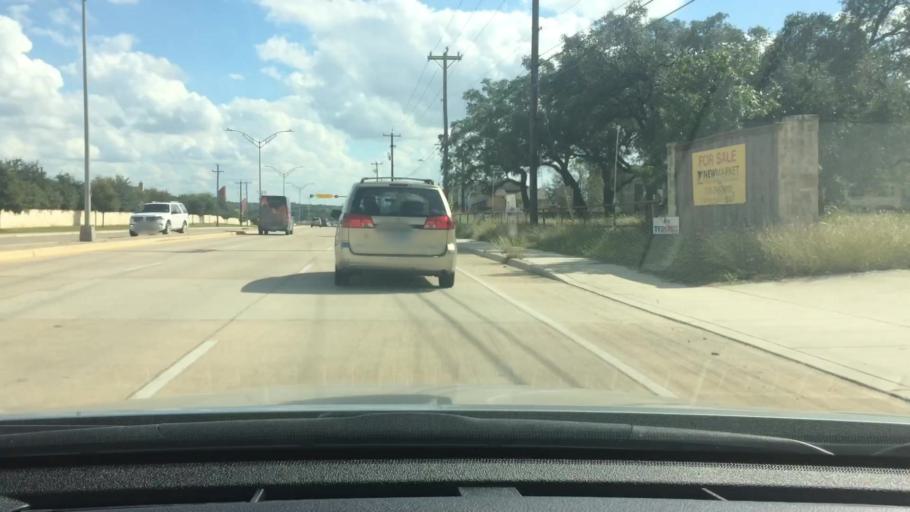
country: US
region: Texas
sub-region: Bexar County
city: Hollywood Park
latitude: 29.6101
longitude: -98.4203
